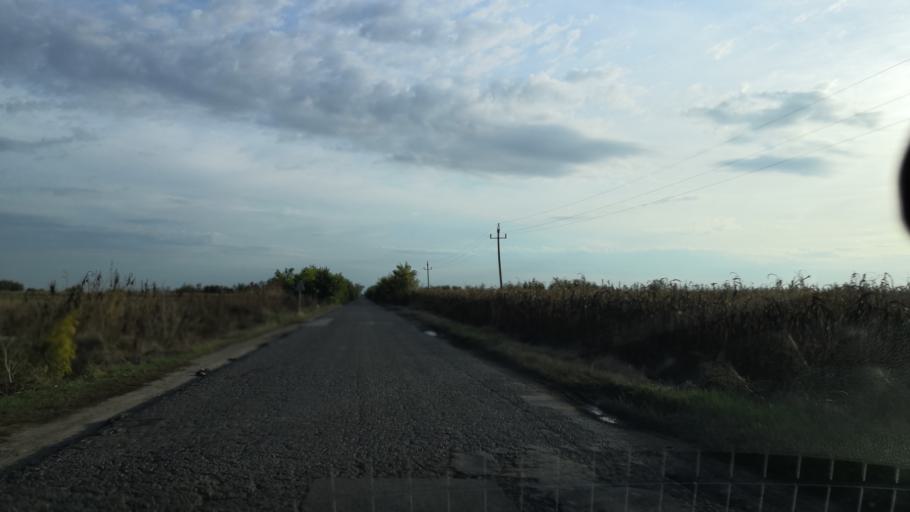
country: RS
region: Autonomna Pokrajina Vojvodina
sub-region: Sremski Okrug
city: Stara Pazova
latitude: 45.0264
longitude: 20.1712
